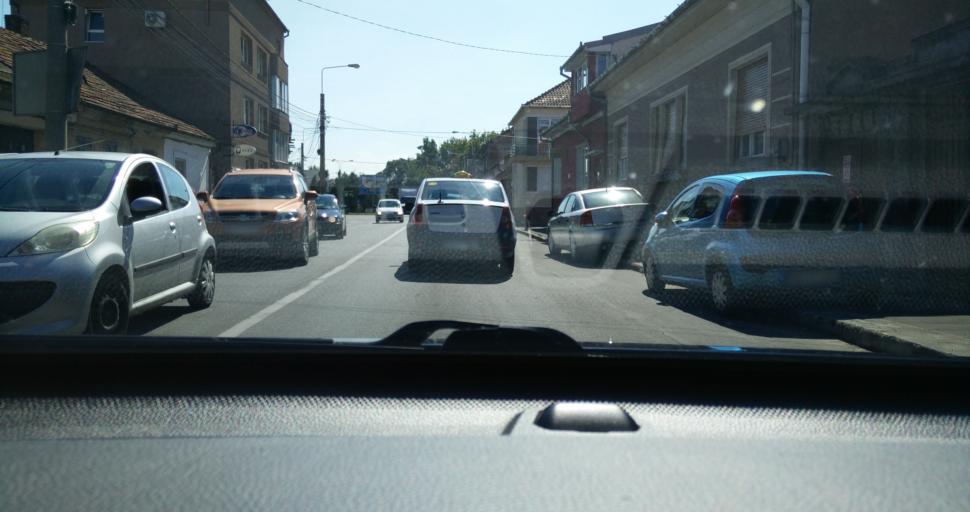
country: RO
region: Bihor
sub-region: Comuna Biharea
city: Oradea
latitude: 47.0500
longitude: 21.9272
